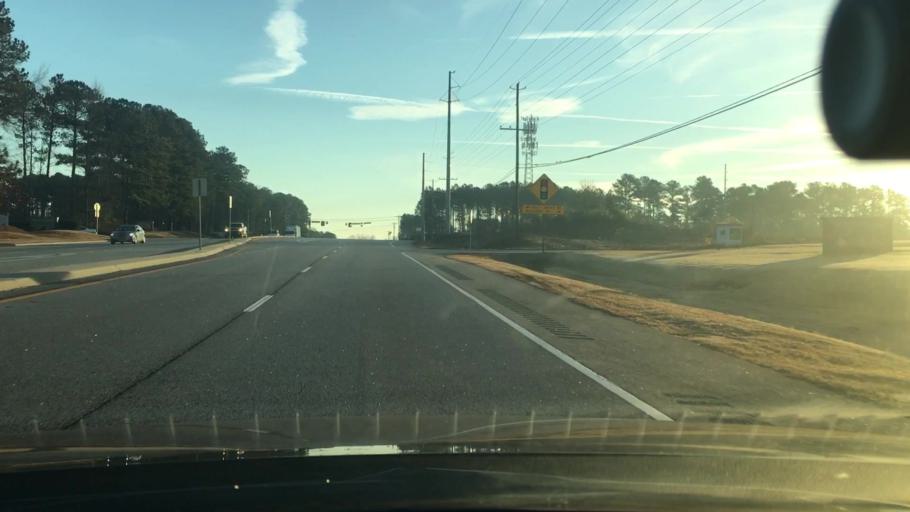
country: US
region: Georgia
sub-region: Coweta County
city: Senoia
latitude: 33.3418
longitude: -84.5366
